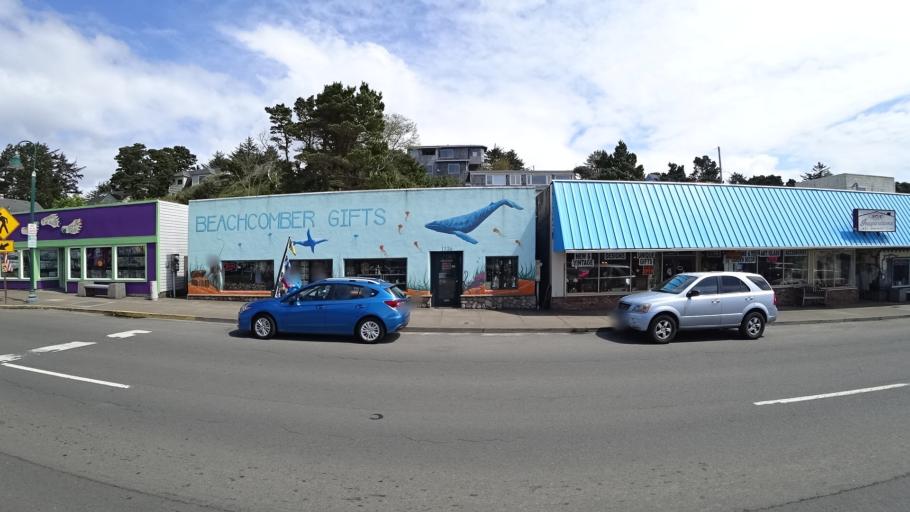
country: US
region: Oregon
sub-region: Lincoln County
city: Lincoln City
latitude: 44.9776
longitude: -124.0114
